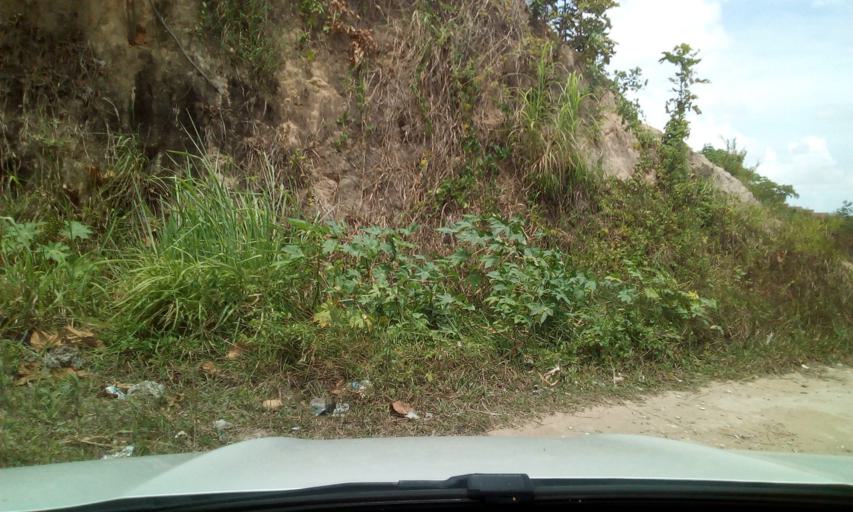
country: BR
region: Paraiba
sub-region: Joao Pessoa
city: Joao Pessoa
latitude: -7.1707
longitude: -34.8827
